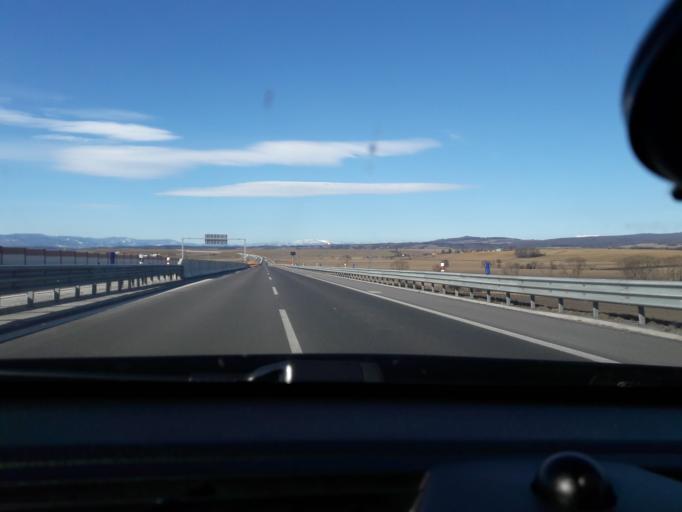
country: SK
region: Banskobystricky
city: Detva
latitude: 48.5517
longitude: 19.3235
